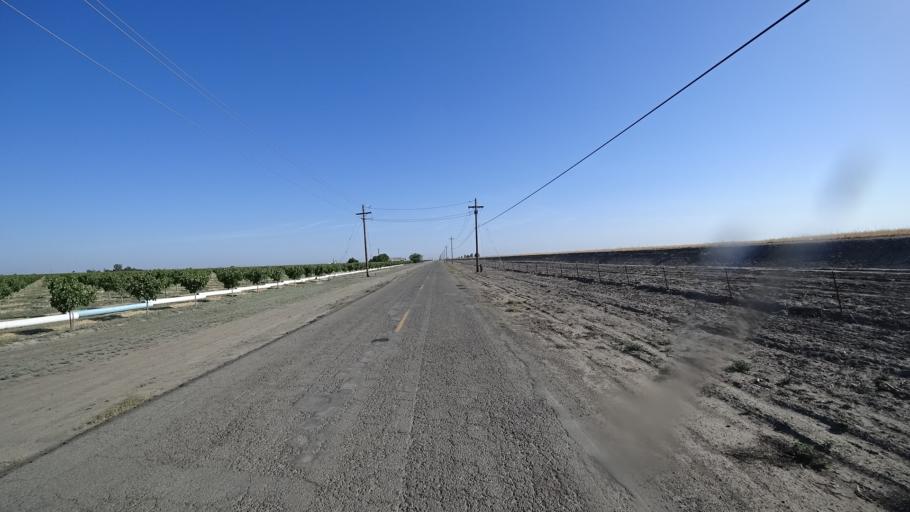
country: US
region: California
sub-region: Kings County
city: Corcoran
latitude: 36.1242
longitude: -119.5543
